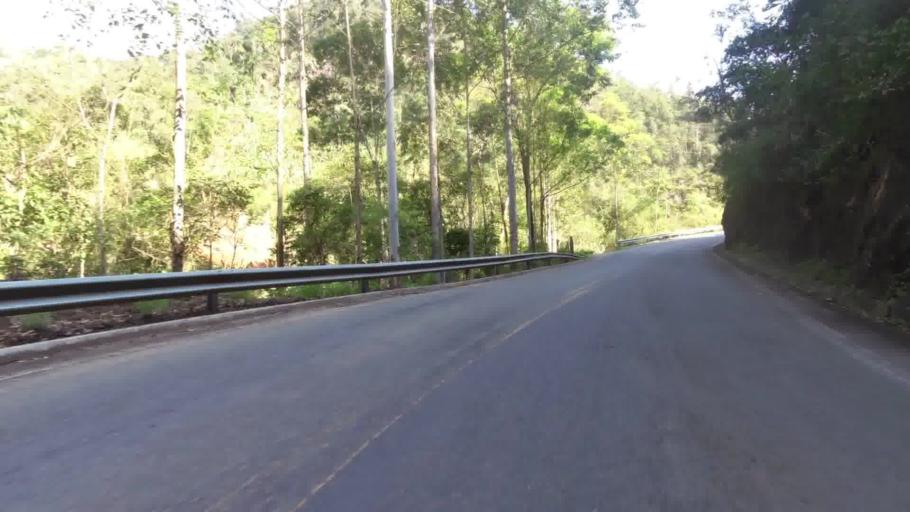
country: BR
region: Espirito Santo
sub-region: Alfredo Chaves
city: Alfredo Chaves
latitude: -20.5772
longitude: -40.8037
